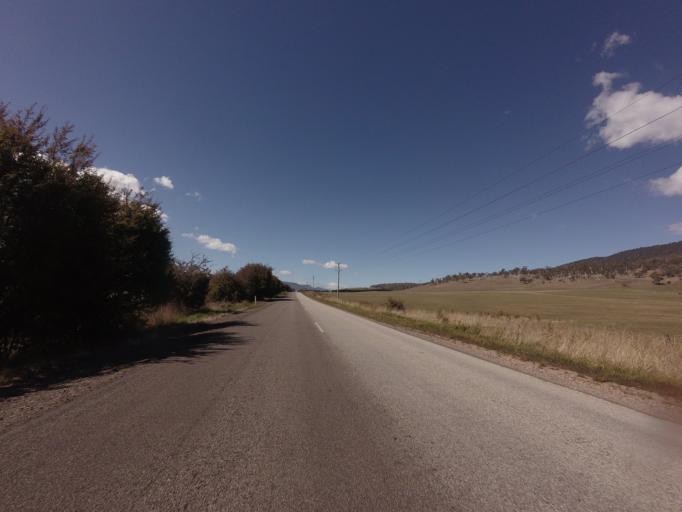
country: AU
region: Tasmania
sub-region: Break O'Day
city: St Helens
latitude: -41.6261
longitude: 147.9929
